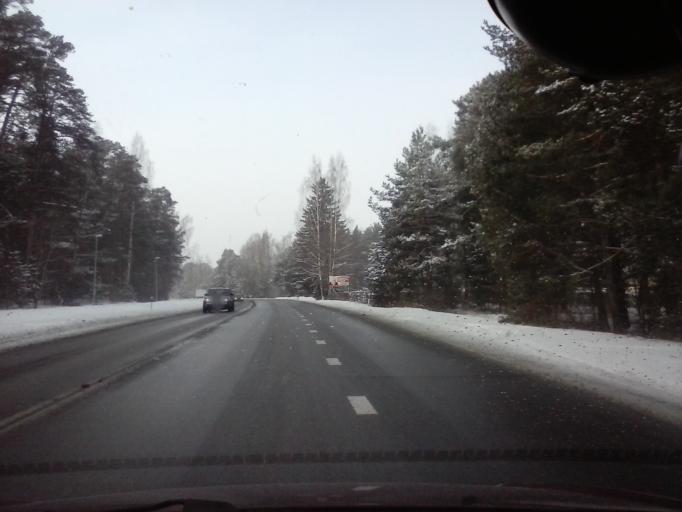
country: EE
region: Paernumaa
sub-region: Paernu linn
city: Parnu
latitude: 58.3773
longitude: 24.5644
